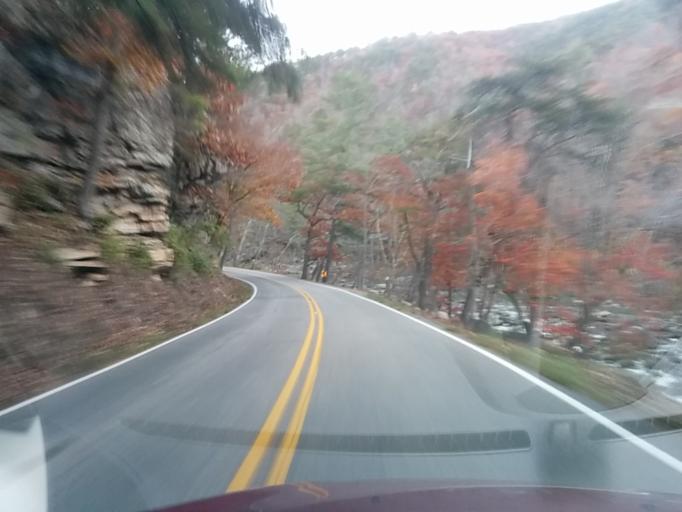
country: US
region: Virginia
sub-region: Rockbridge County
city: East Lexington
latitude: 37.9375
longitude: -79.4526
